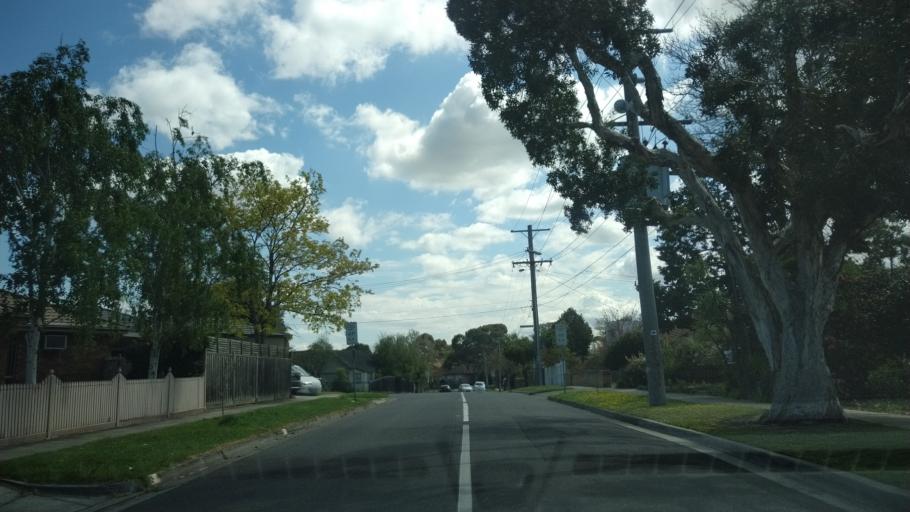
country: AU
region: Victoria
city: Highett
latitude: -37.9555
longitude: 145.0462
